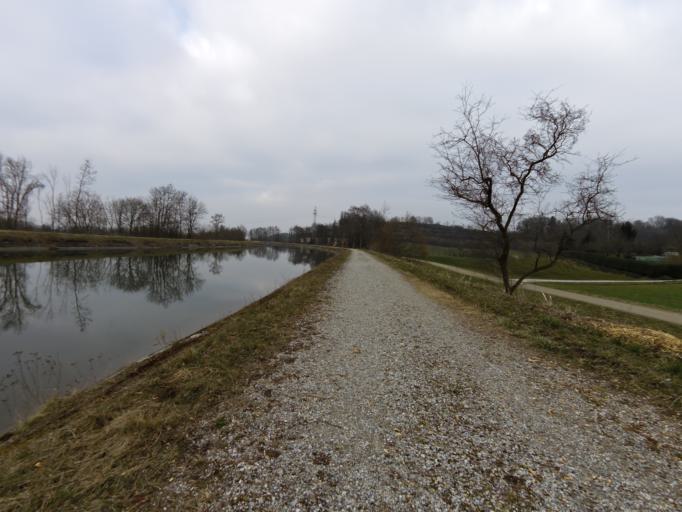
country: DE
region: Bavaria
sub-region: Upper Bavaria
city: Langenpreising
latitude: 48.4355
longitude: 11.9912
